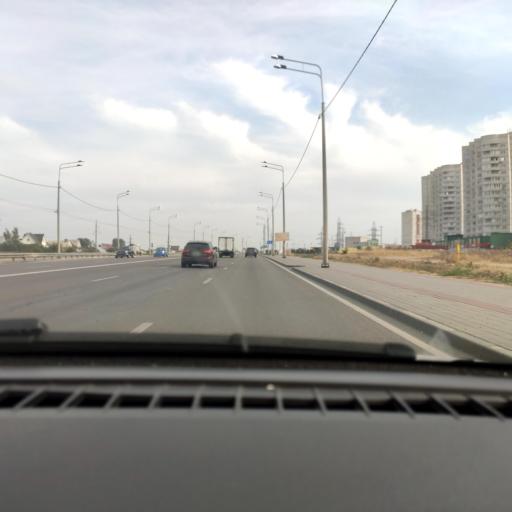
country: RU
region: Voronezj
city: Podgornoye
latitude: 51.7221
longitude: 39.1537
